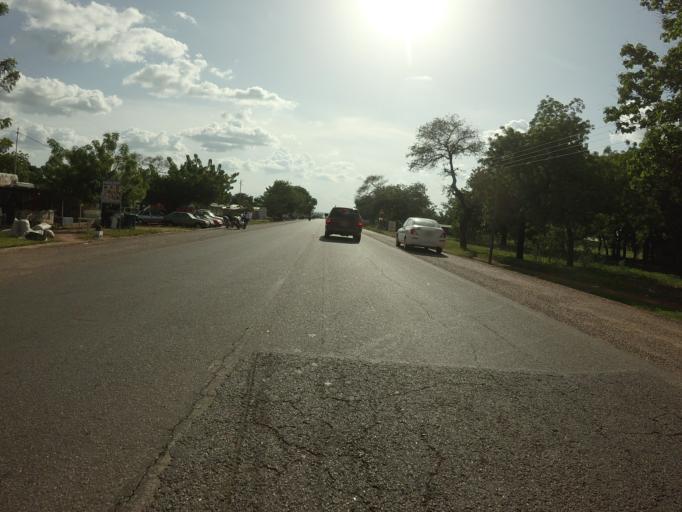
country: GH
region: Upper East
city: Bolgatanga
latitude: 10.8028
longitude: -0.8671
